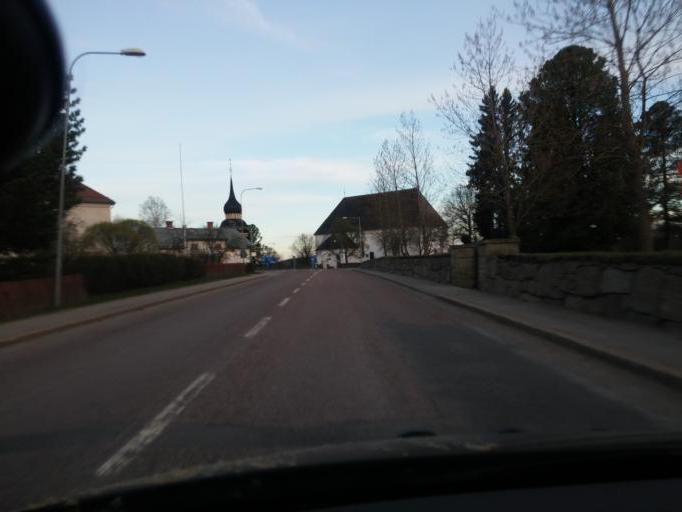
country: SE
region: Gaevleborg
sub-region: Ljusdals Kommun
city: Ljusdal
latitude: 61.8300
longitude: 16.0711
